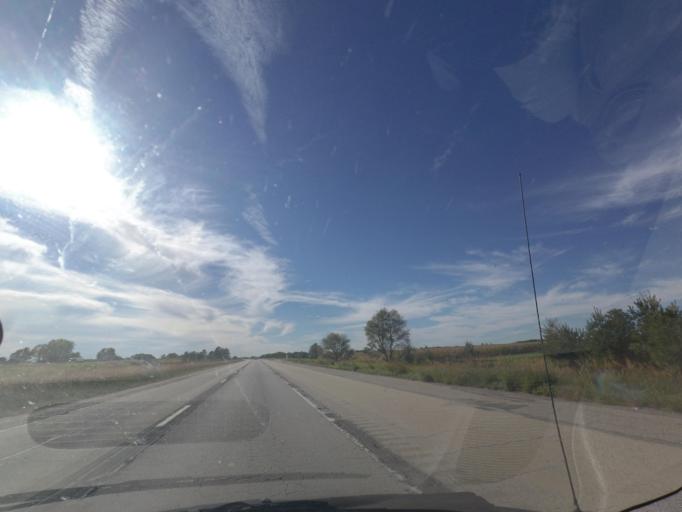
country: US
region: Illinois
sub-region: Macon County
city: Forsyth
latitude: 39.9081
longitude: -88.9780
